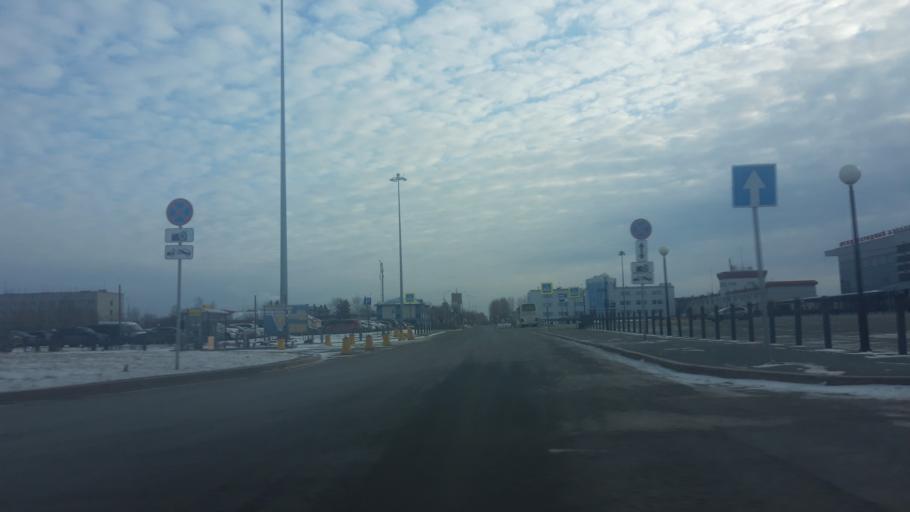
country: RU
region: Tjumen
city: Moskovskiy
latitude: 57.1827
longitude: 65.3488
